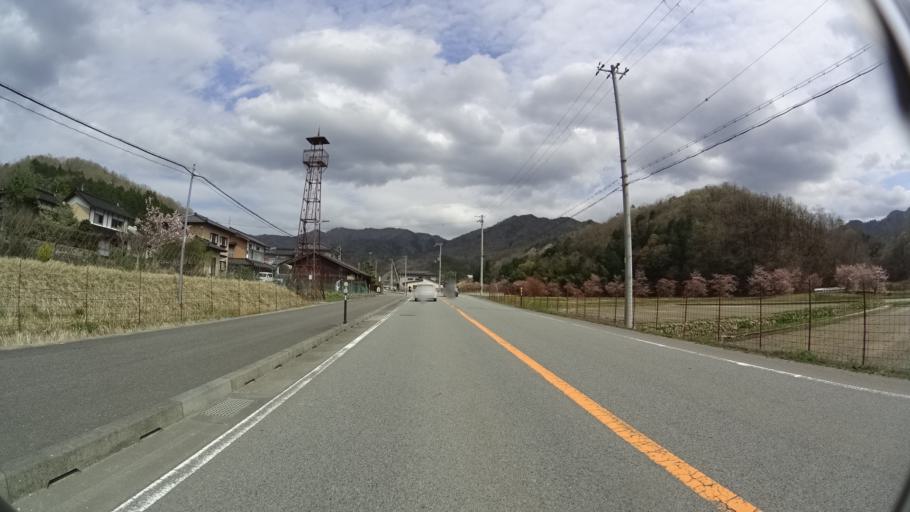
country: JP
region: Hyogo
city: Toyooka
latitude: 35.5020
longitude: 134.8811
